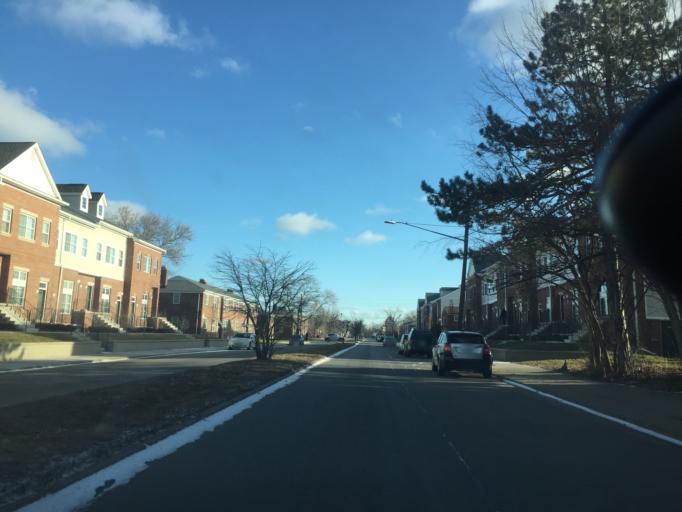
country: US
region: Michigan
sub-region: Wayne County
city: Highland Park
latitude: 42.3924
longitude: -83.1373
